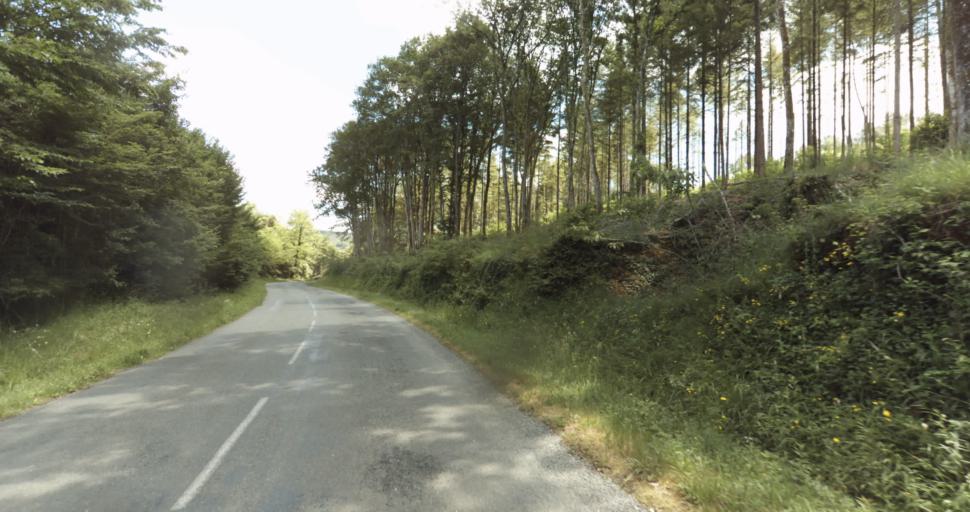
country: FR
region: Aquitaine
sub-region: Departement de la Dordogne
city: Beaumont-du-Perigord
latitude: 44.8122
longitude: 0.8621
